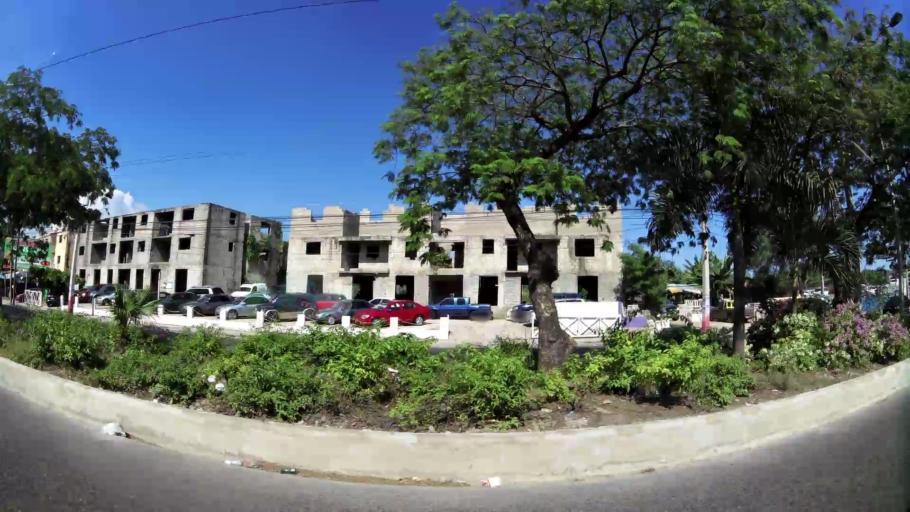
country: DO
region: San Cristobal
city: El Carril
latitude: 18.4617
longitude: -69.9927
